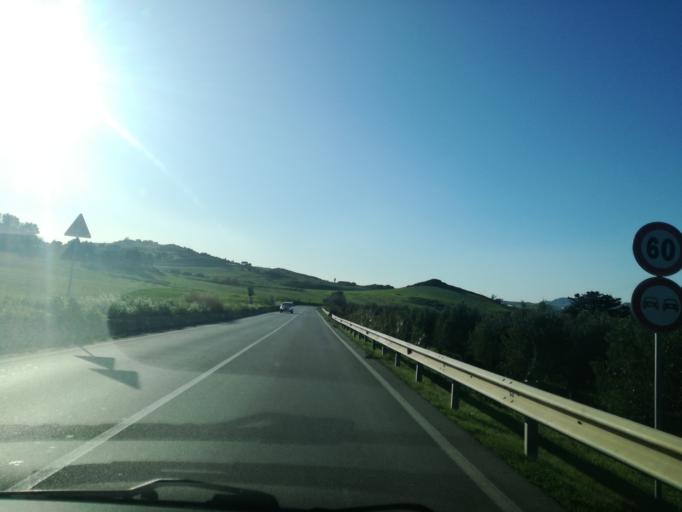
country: IT
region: Sicily
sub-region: Provincia di Caltanissetta
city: Butera
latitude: 37.1133
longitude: 14.1521
